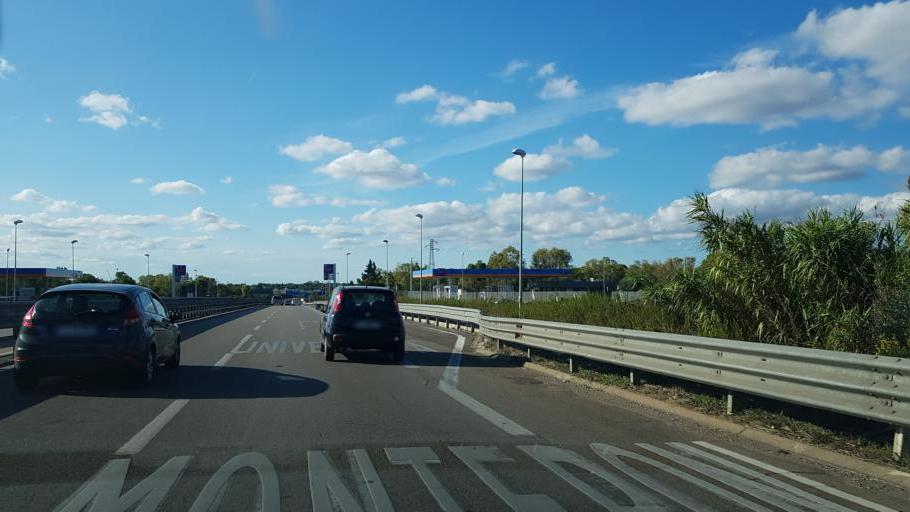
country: IT
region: Apulia
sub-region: Provincia di Lecce
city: Lequile
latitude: 40.3309
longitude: 18.1389
